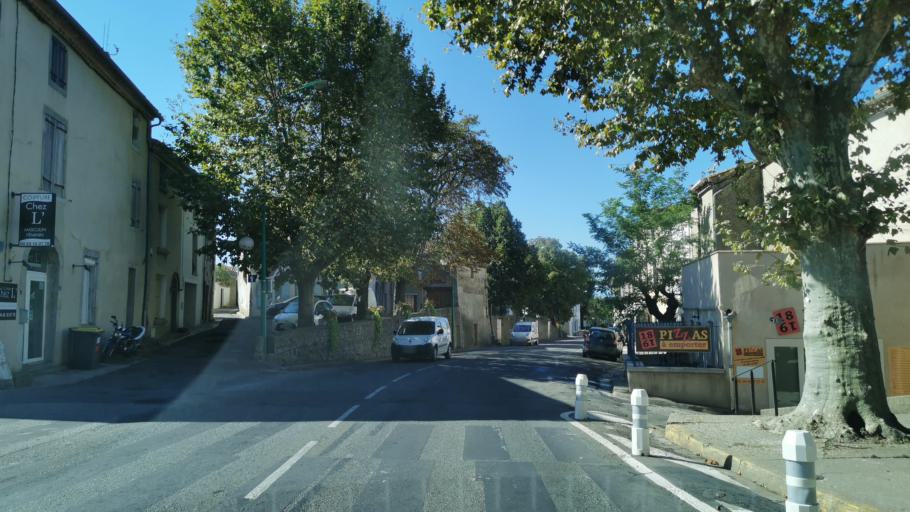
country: FR
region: Languedoc-Roussillon
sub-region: Departement de l'Aude
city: Conques-sur-Orbiel
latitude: 43.2573
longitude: 2.4120
